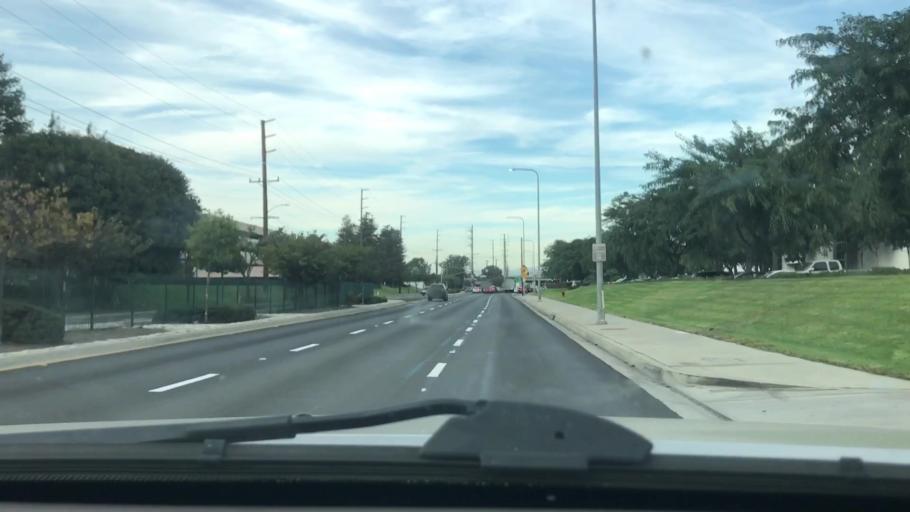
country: US
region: California
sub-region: Los Angeles County
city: Gardena
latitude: 33.8555
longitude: -118.3093
